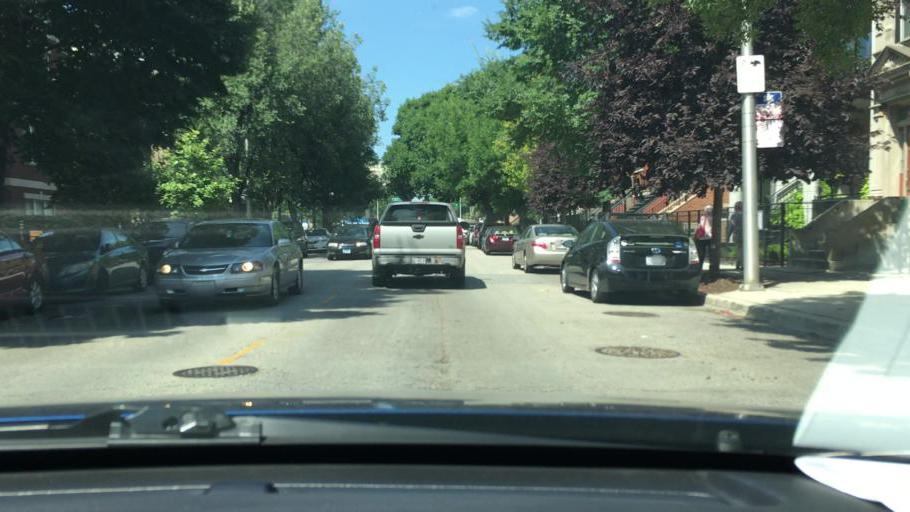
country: US
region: Illinois
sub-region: Cook County
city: Chicago
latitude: 41.8682
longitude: -87.6567
